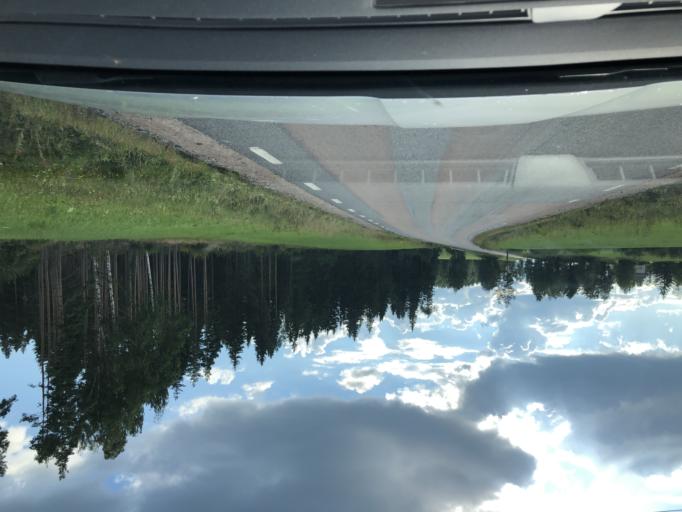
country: SE
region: Vaesternorrland
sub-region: Solleftea Kommun
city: Solleftea
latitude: 63.2008
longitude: 17.1053
